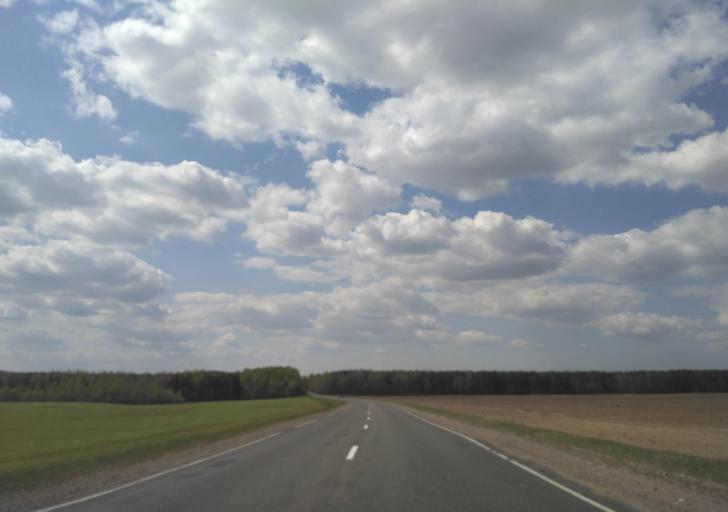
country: BY
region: Minsk
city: Vilyeyka
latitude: 54.5176
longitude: 27.0191
